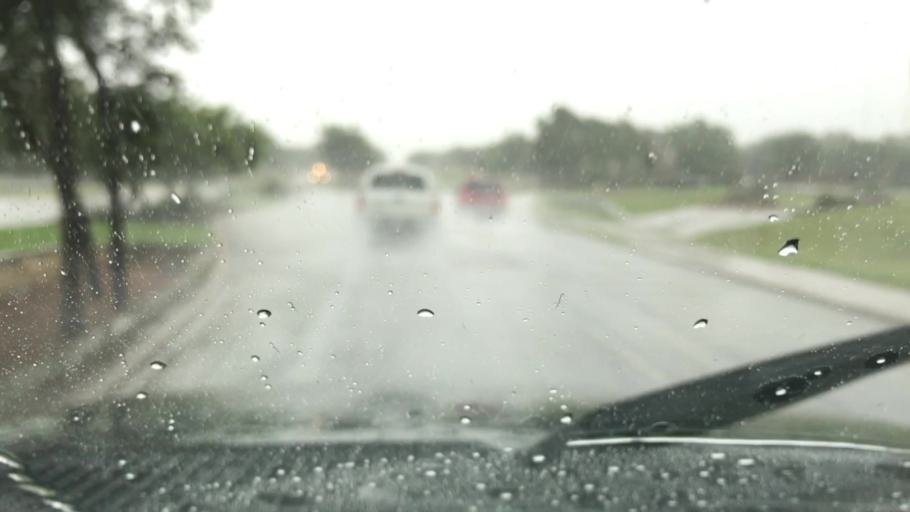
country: US
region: Texas
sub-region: Williamson County
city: Leander
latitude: 30.5361
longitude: -97.8609
